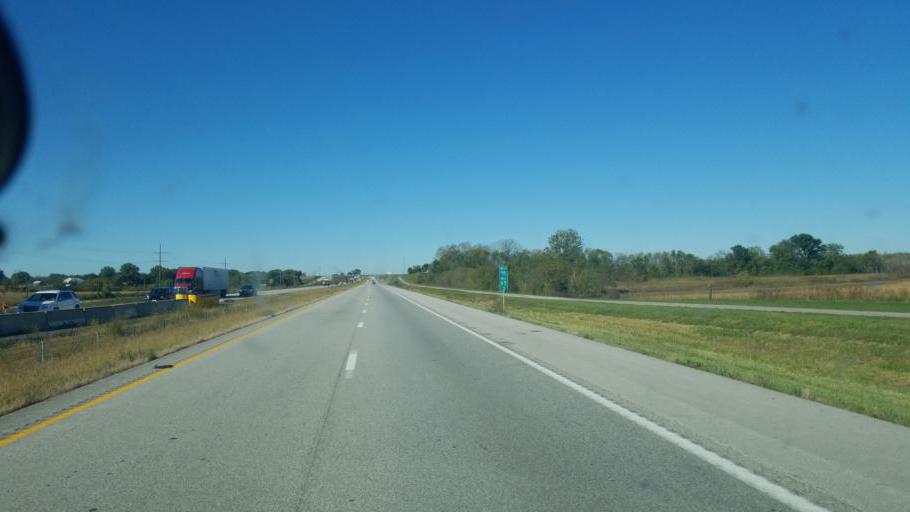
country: US
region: Missouri
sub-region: Saline County
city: Sweet Springs
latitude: 38.9782
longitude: -93.4463
